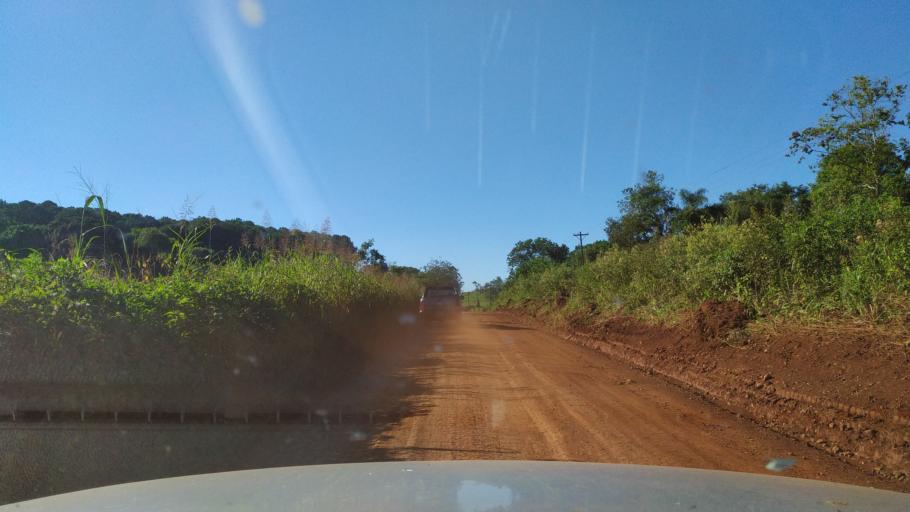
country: AR
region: Misiones
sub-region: Departamento de Montecarlo
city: Montecarlo
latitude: -26.6164
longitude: -54.6973
